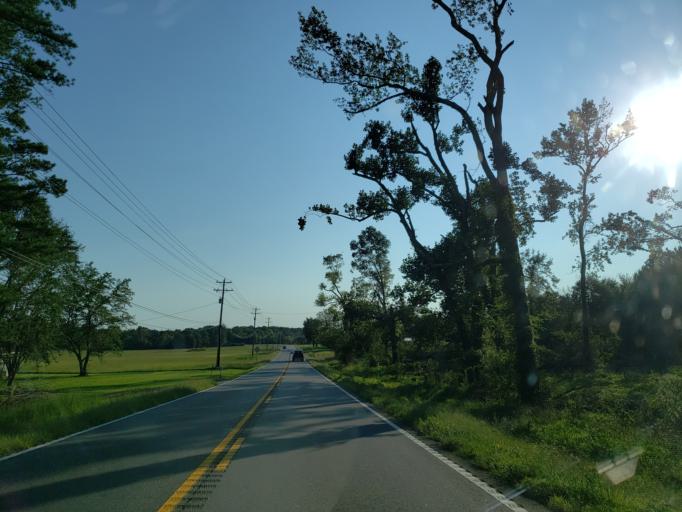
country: US
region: Georgia
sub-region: Murray County
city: Chatsworth
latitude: 34.8074
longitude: -84.8187
